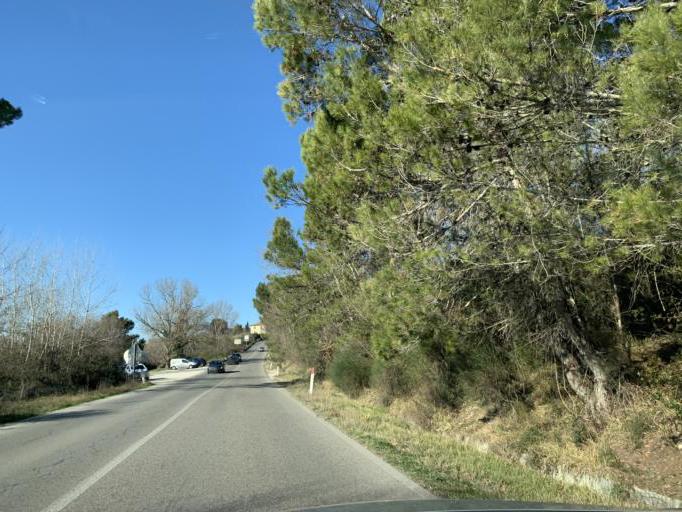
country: IT
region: Umbria
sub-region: Provincia di Terni
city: Fornole
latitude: 42.5394
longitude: 12.4730
